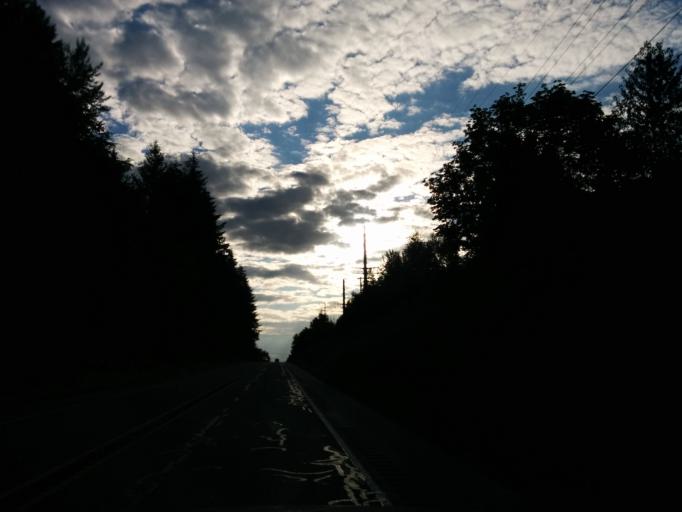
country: US
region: Washington
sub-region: Snohomish County
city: Sultan
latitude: 47.8691
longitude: -121.7691
